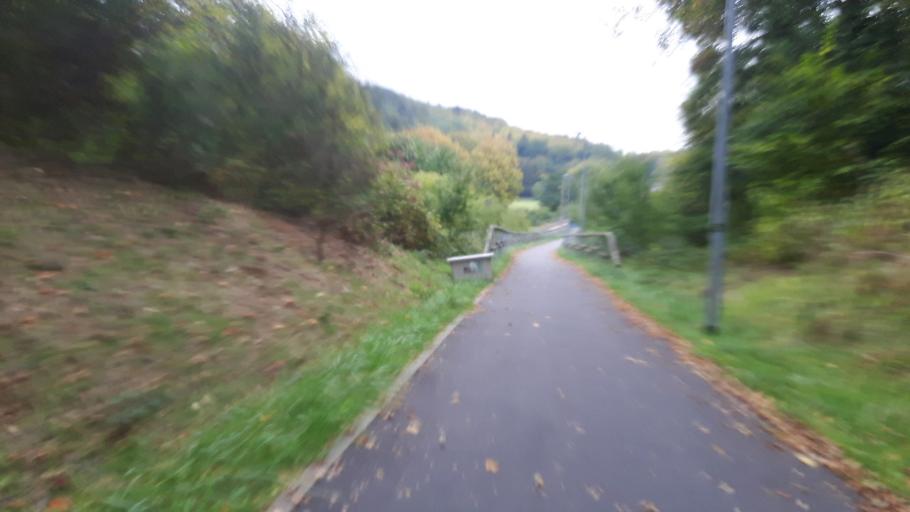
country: DE
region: North Rhine-Westphalia
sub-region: Regierungsbezirk Koln
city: Eitorf
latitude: 50.7734
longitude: 7.3796
